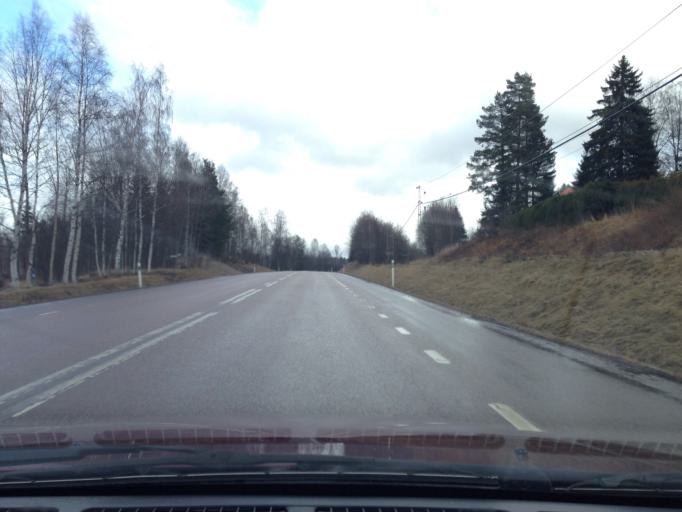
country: SE
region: Dalarna
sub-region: Ludvika Kommun
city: Ludvika
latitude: 60.1515
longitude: 15.2256
